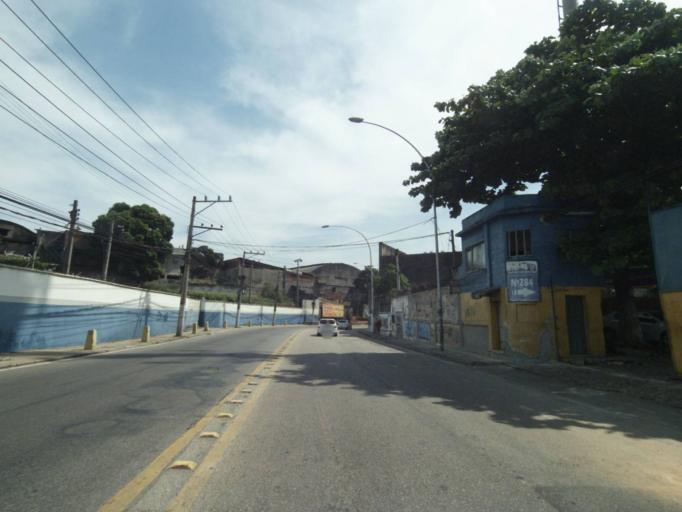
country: BR
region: Rio de Janeiro
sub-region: Rio De Janeiro
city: Rio de Janeiro
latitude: -22.8705
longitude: -43.2489
